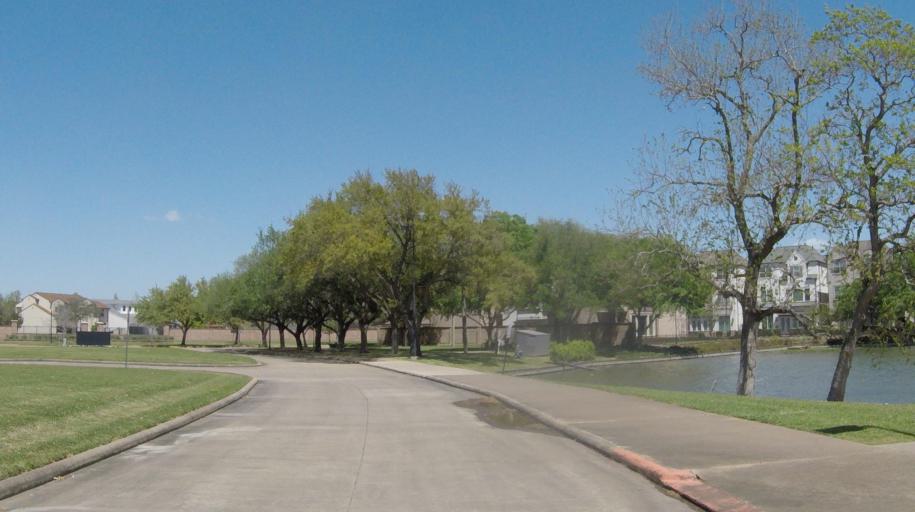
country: US
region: Texas
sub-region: Fort Bend County
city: Sugar Land
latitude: 29.6064
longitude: -95.6237
